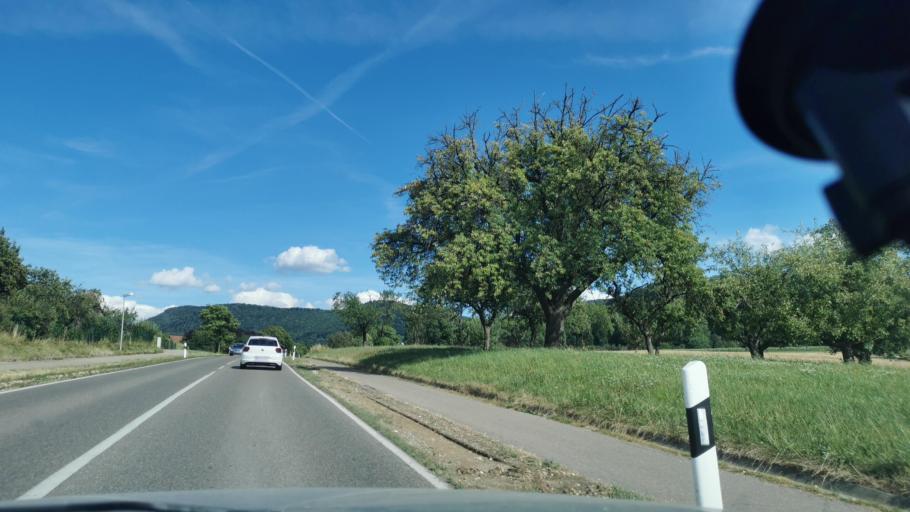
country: DE
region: Baden-Wuerttemberg
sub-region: Regierungsbezirk Stuttgart
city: Heubach
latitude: 48.7956
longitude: 9.9128
